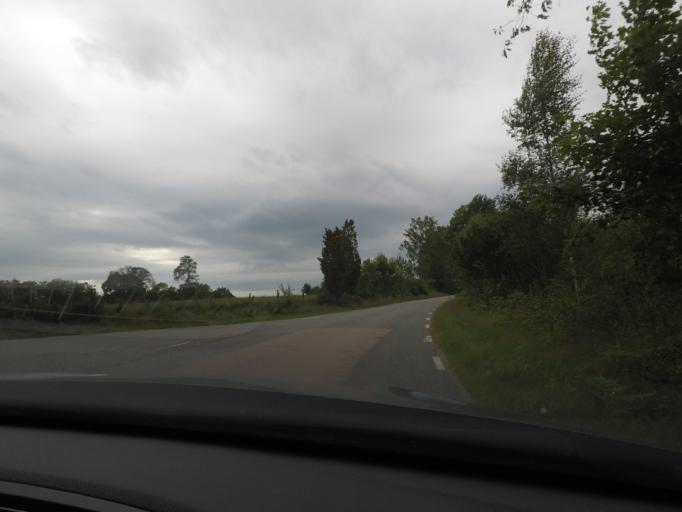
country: SE
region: Kronoberg
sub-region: Markaryds Kommun
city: Stromsnasbruk
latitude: 56.4200
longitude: 13.7264
